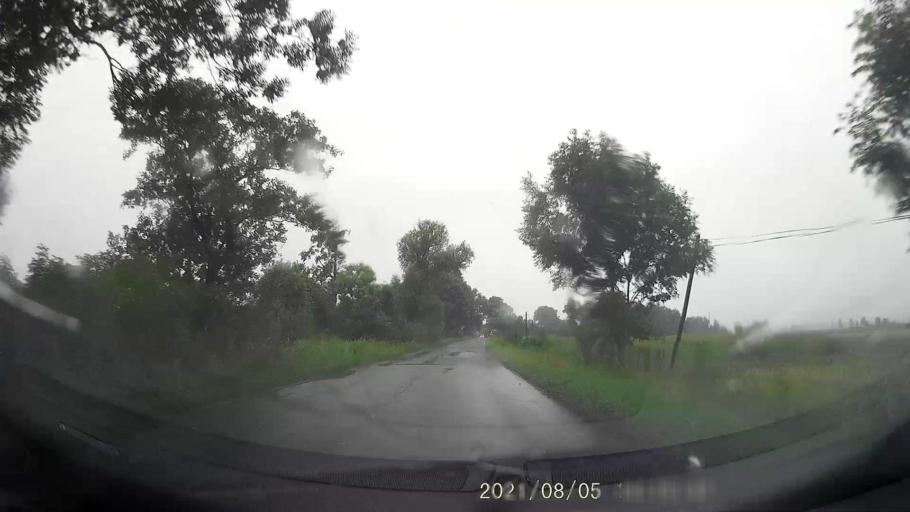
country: PL
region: Opole Voivodeship
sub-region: Powiat prudnicki
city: Biala
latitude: 50.4612
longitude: 17.7304
